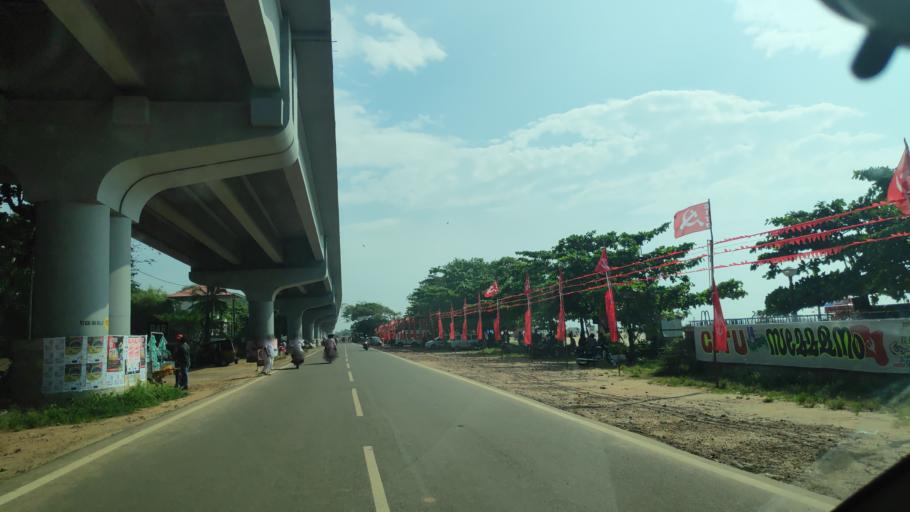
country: IN
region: Kerala
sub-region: Alappuzha
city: Alleppey
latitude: 9.4942
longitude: 76.3184
